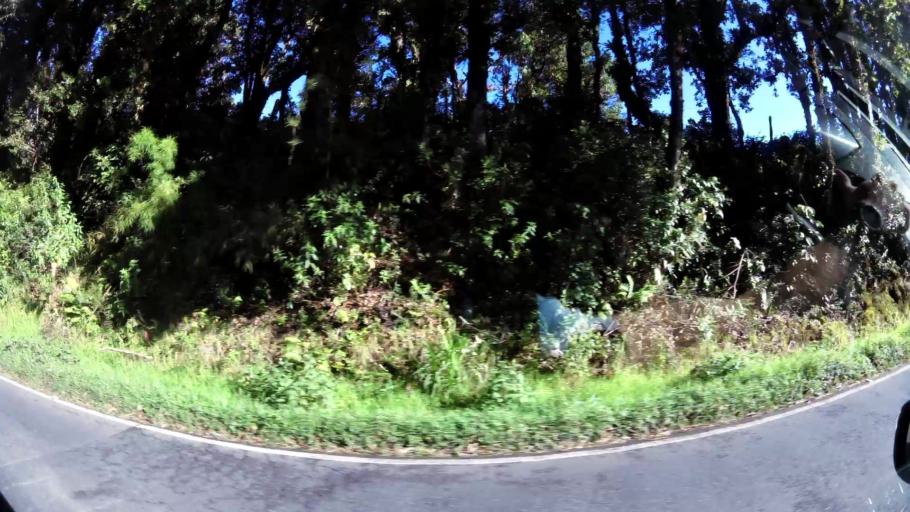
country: CR
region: San Jose
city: San Marcos
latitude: 9.6978
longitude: -83.9323
